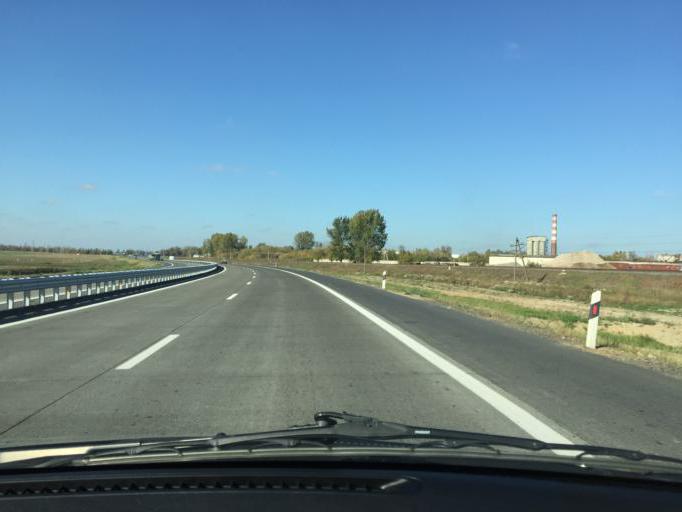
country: BY
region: Minsk
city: Slutsk
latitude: 52.9974
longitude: 27.5063
